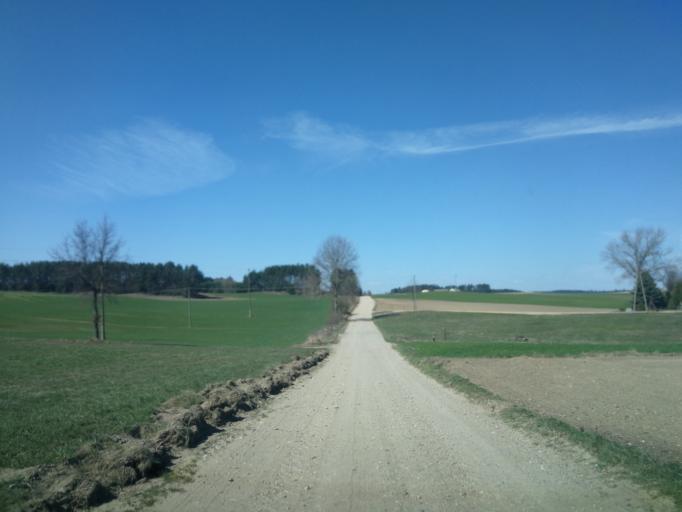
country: PL
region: Warmian-Masurian Voivodeship
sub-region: Powiat dzialdowski
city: Rybno
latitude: 53.4398
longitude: 19.9433
